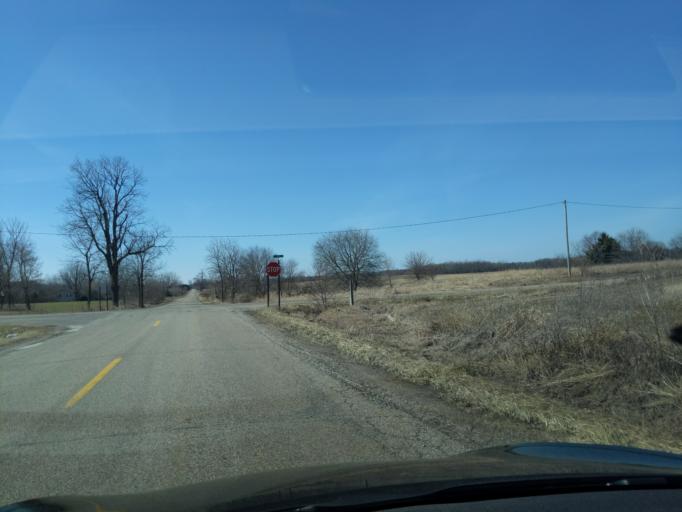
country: US
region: Michigan
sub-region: Ionia County
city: Portland
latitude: 42.7267
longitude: -84.9555
